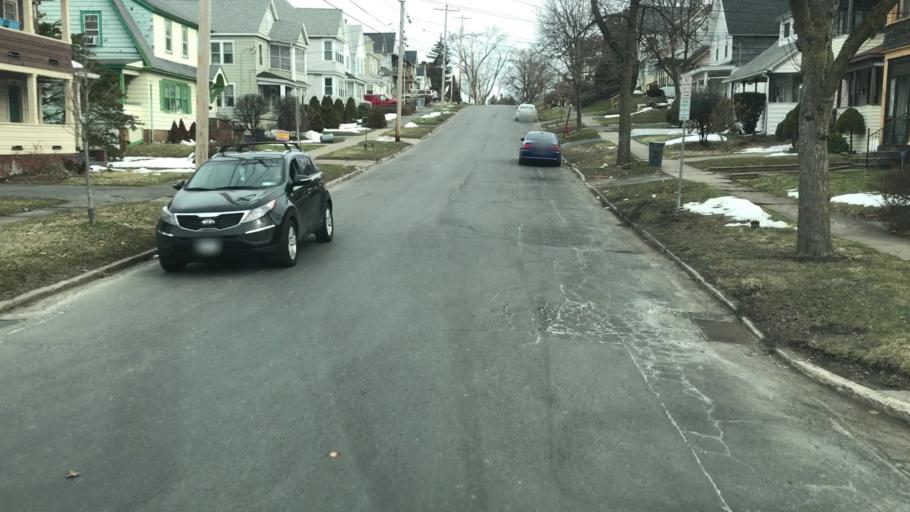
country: US
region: New York
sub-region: Onondaga County
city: Lyncourt
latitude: 43.0694
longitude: -76.1365
